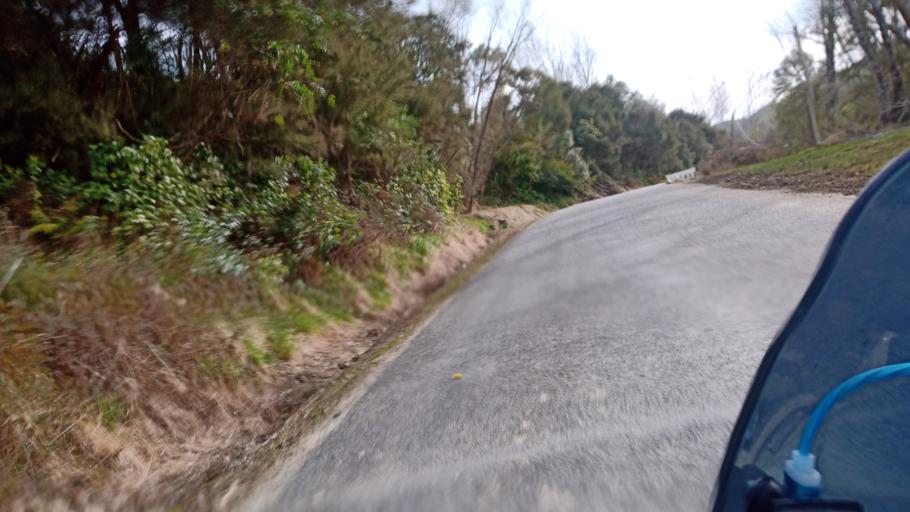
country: NZ
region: Hawke's Bay
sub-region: Wairoa District
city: Wairoa
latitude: -38.8032
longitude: 177.4715
